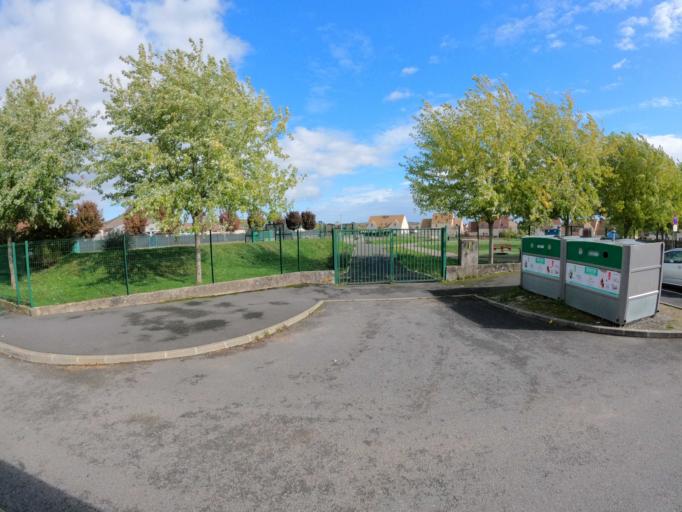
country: FR
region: Ile-de-France
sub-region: Departement de Seine-et-Marne
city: Montry
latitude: 48.8835
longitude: 2.8326
